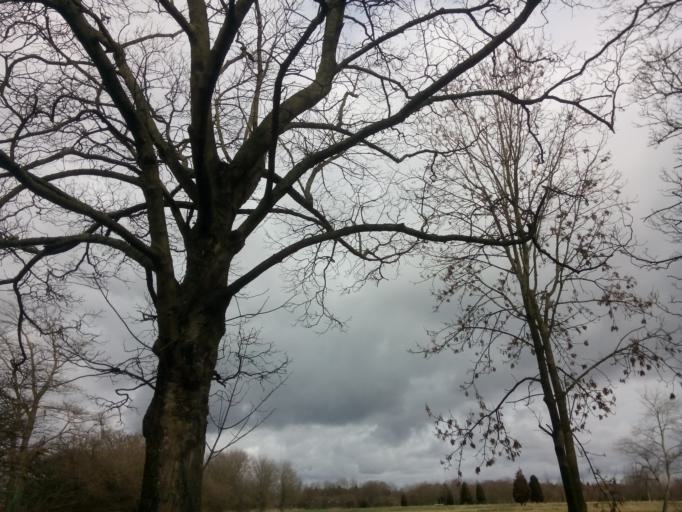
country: GB
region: England
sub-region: County Durham
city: Durham
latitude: 54.7612
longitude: -1.5921
